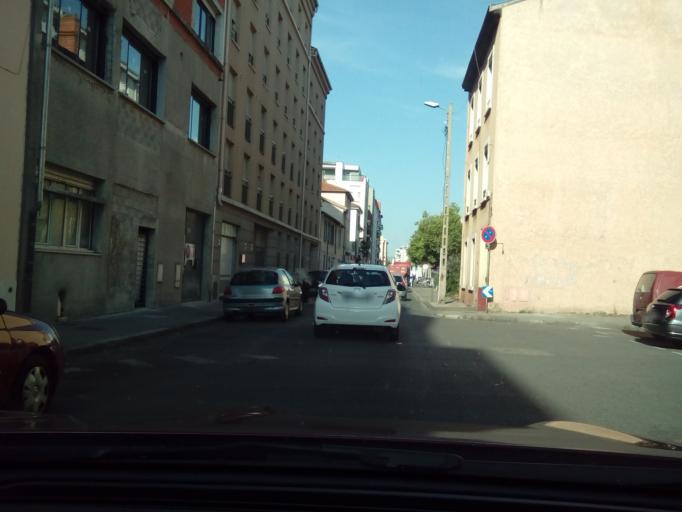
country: FR
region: Rhone-Alpes
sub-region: Departement du Rhone
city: Villeurbanne
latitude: 45.7540
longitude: 4.8928
